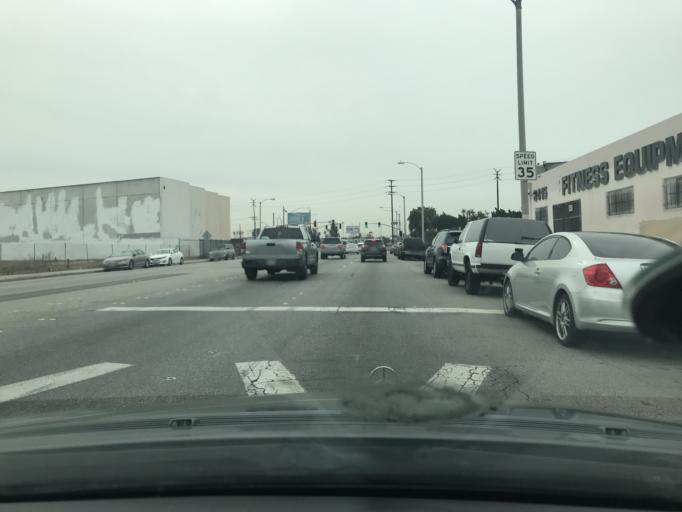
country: US
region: California
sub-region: Los Angeles County
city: Cudahy
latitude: 33.9569
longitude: -118.1845
